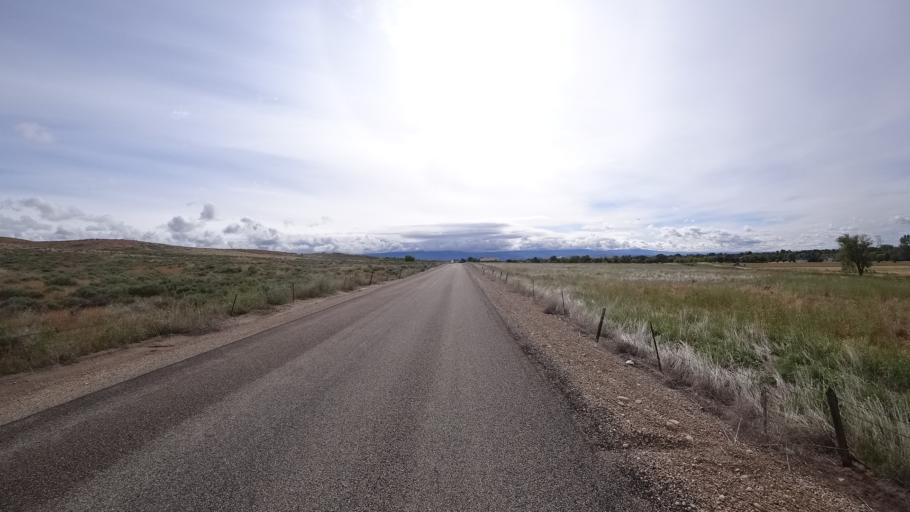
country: US
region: Idaho
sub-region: Ada County
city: Eagle
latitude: 43.7355
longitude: -116.4118
